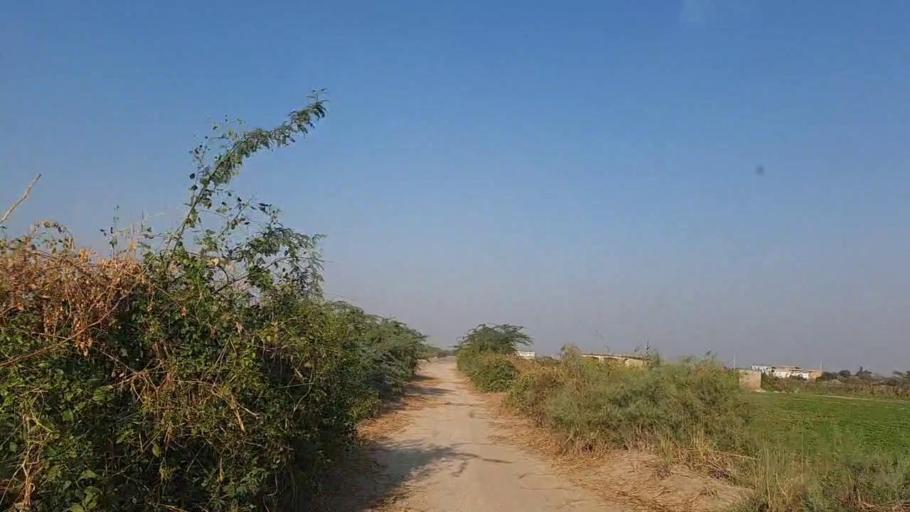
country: PK
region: Sindh
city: Thatta
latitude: 24.7248
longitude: 67.9483
